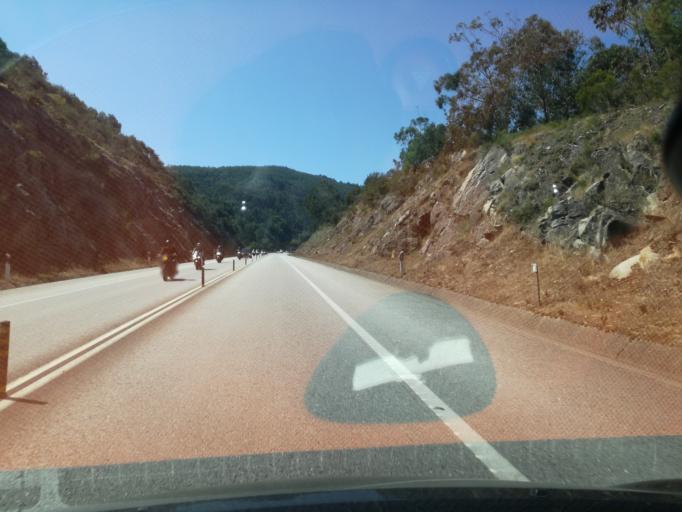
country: PT
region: Viana do Castelo
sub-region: Vila Nova de Cerveira
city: Vila Nova de Cerveira
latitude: 41.8907
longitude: -8.7735
